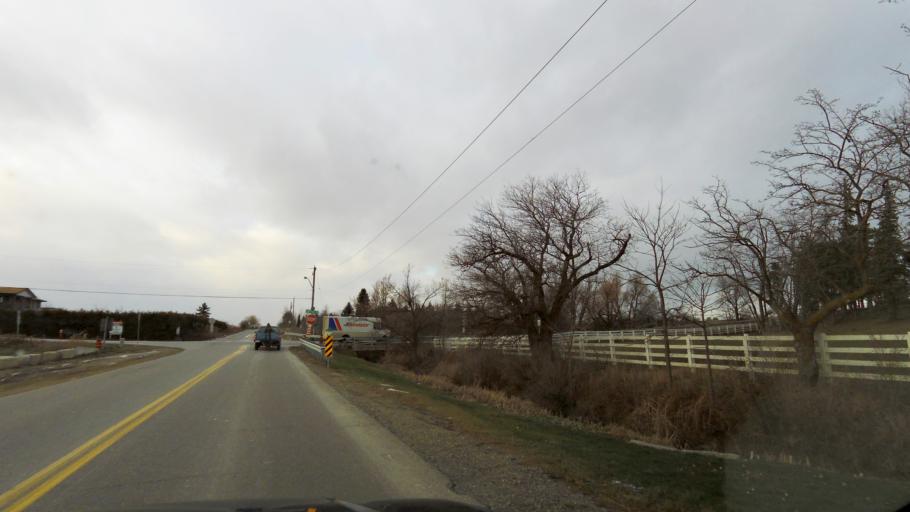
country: CA
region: Ontario
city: Brampton
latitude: 43.8209
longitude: -79.7053
